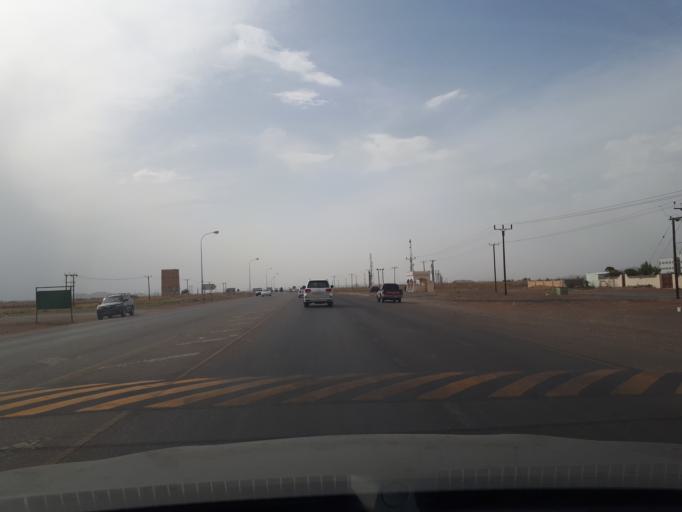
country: OM
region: Ash Sharqiyah
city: Badiyah
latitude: 22.5054
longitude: 58.7462
